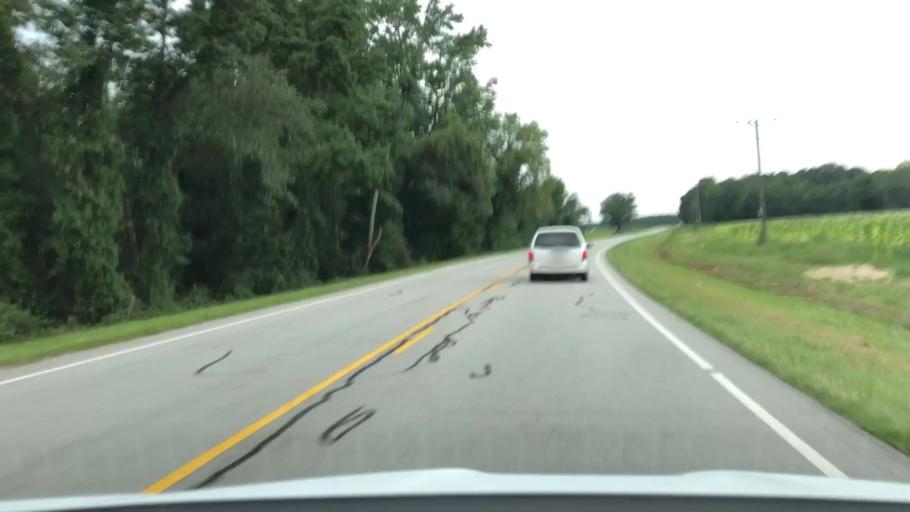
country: US
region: North Carolina
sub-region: Jones County
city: Trenton
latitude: 35.0784
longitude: -77.4234
